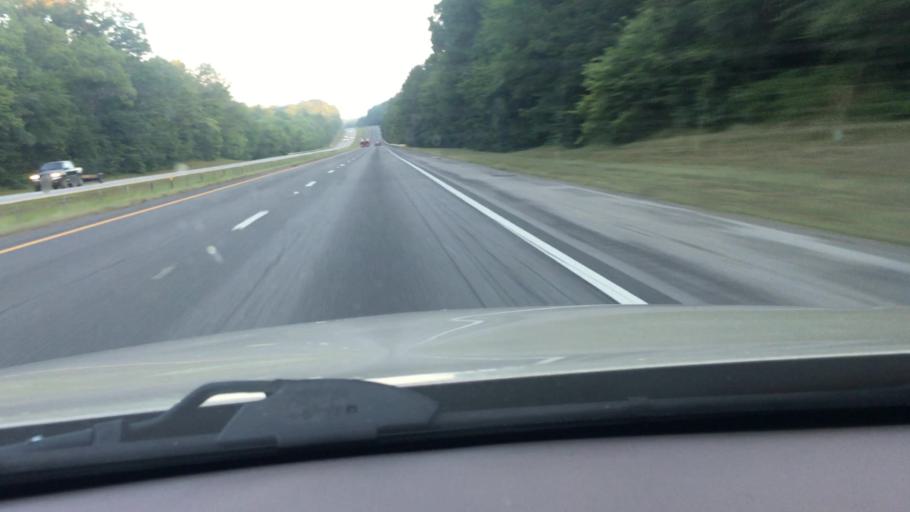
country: US
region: South Carolina
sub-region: Lexington County
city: Chapin
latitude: 34.1677
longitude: -81.2943
